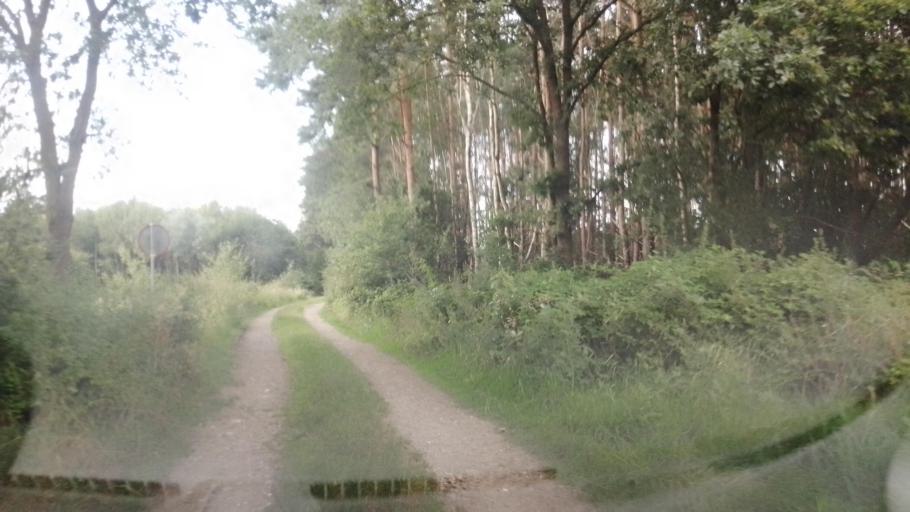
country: NL
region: Limburg
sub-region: Gemeente Venlo
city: Venlo
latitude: 51.4103
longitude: 6.2068
